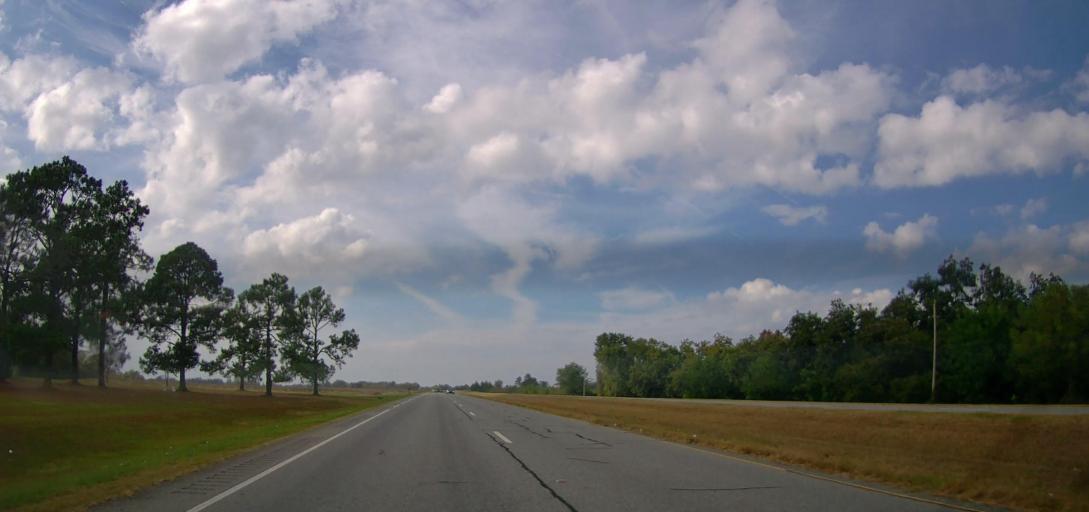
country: US
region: Georgia
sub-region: Mitchell County
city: Pelham
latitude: 31.1075
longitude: -84.1156
